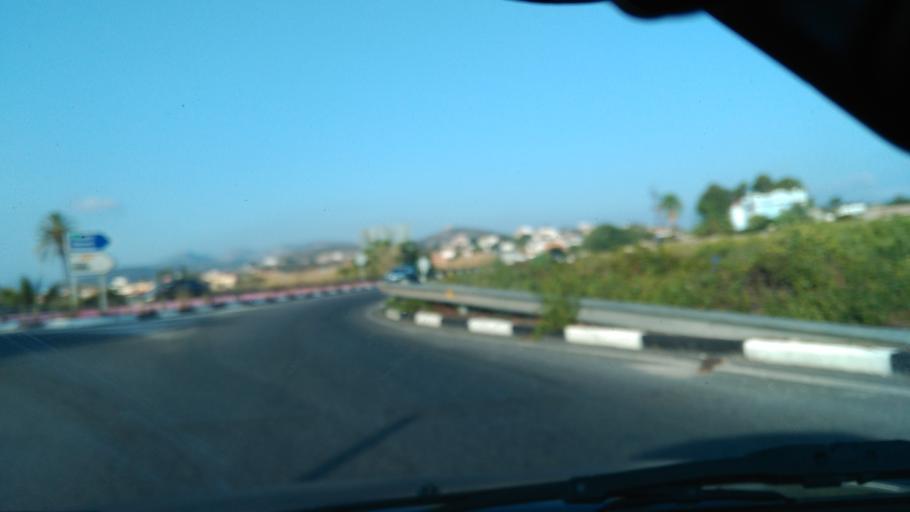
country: ES
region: Valencia
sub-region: Provincia de Alicante
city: Gata de Gorgos
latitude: 38.7833
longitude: 0.0913
